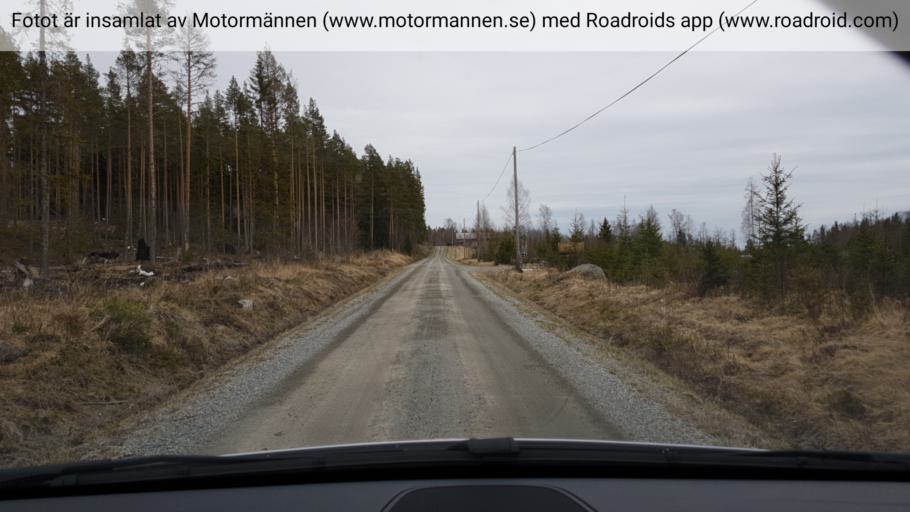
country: SE
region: Jaemtland
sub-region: Bergs Kommun
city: Hoverberg
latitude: 62.8354
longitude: 14.5903
